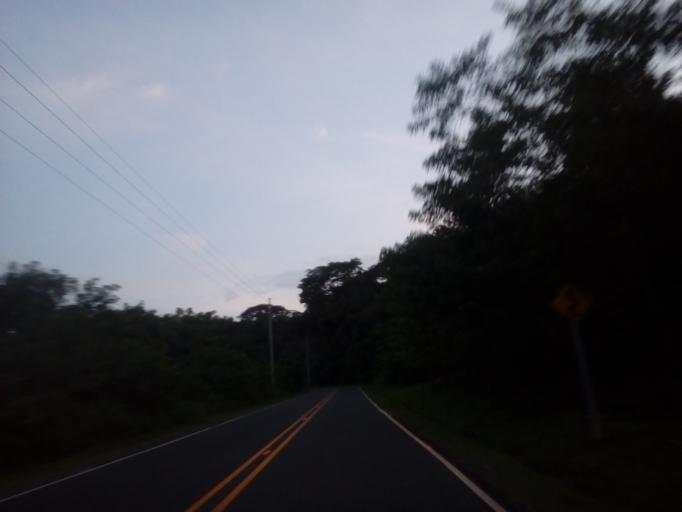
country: CR
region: Guanacaste
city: Hojancha
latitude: 10.0049
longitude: -85.5025
